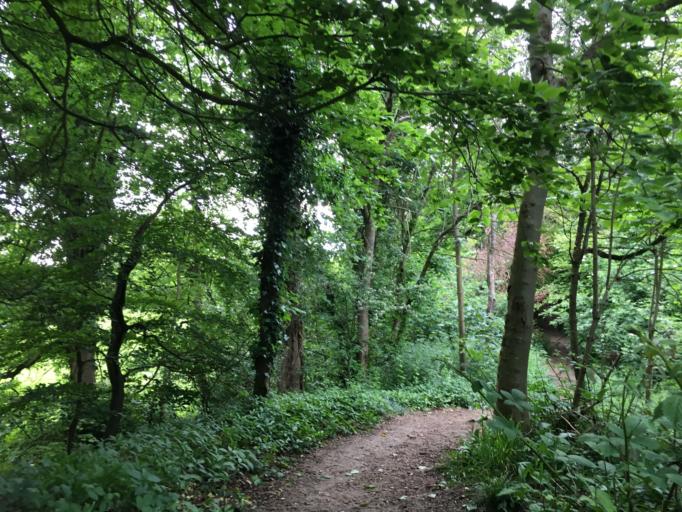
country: GB
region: England
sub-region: Hertfordshire
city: St Albans
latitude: 51.7473
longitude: -0.3577
